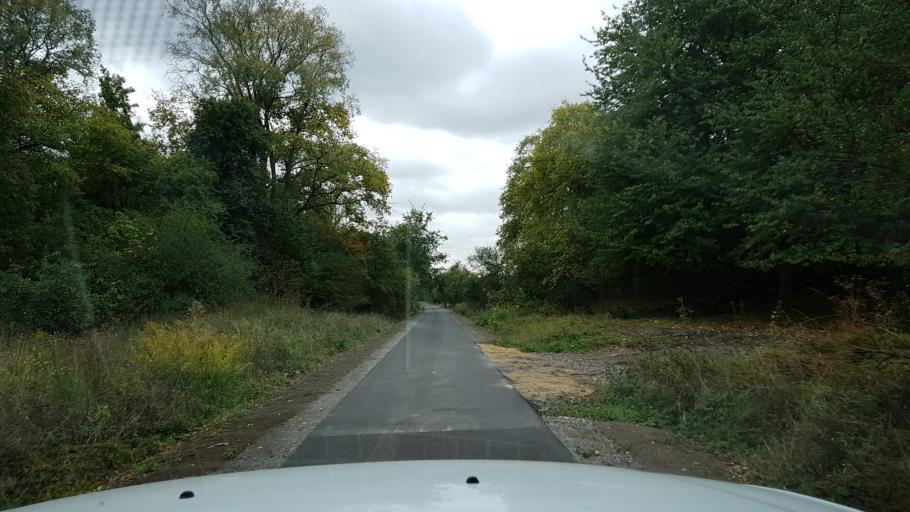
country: PL
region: West Pomeranian Voivodeship
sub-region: Powiat gryfinski
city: Cedynia
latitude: 52.8480
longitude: 14.2838
